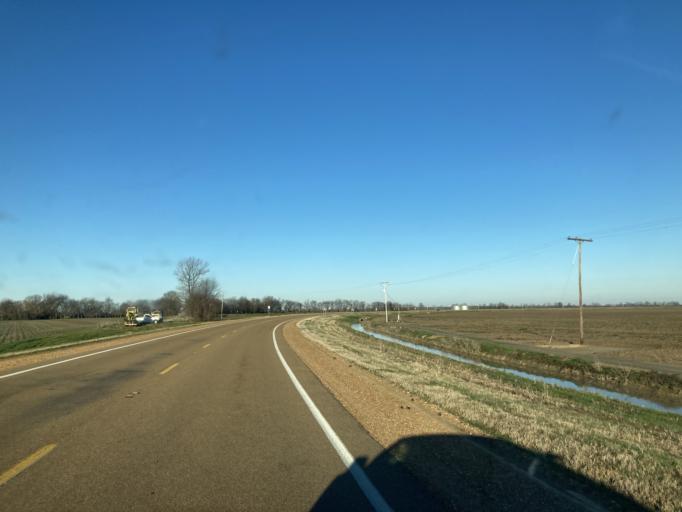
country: US
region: Mississippi
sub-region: Yazoo County
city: Yazoo City
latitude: 32.9267
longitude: -90.5808
